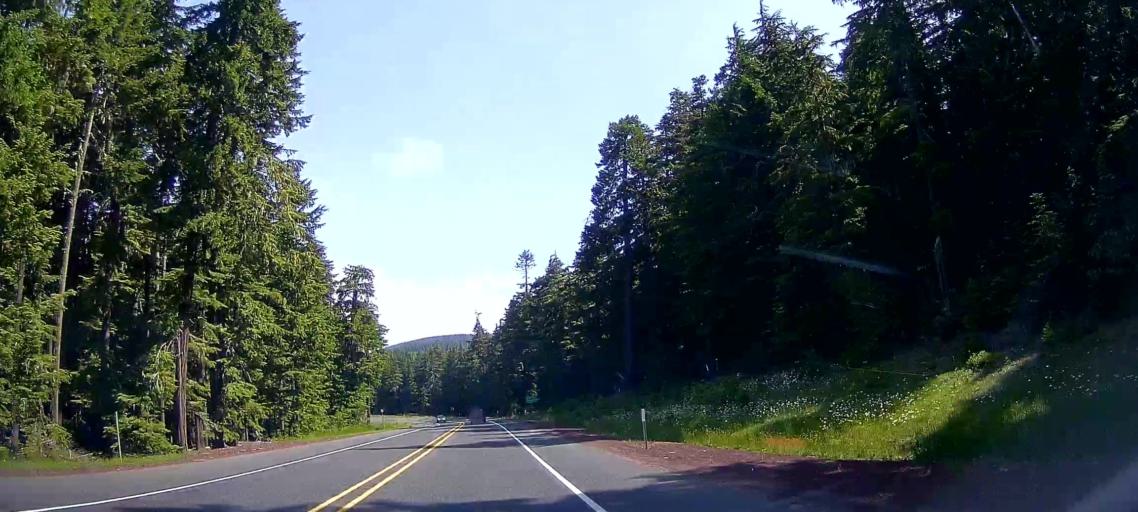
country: US
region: Oregon
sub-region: Clackamas County
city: Mount Hood Village
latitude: 45.1846
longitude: -121.6767
